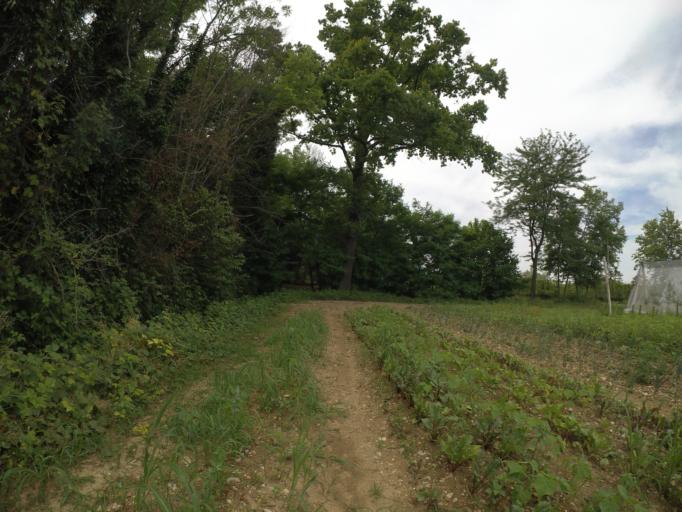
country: IT
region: Friuli Venezia Giulia
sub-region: Provincia di Udine
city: Bertiolo
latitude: 45.9353
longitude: 13.0535
